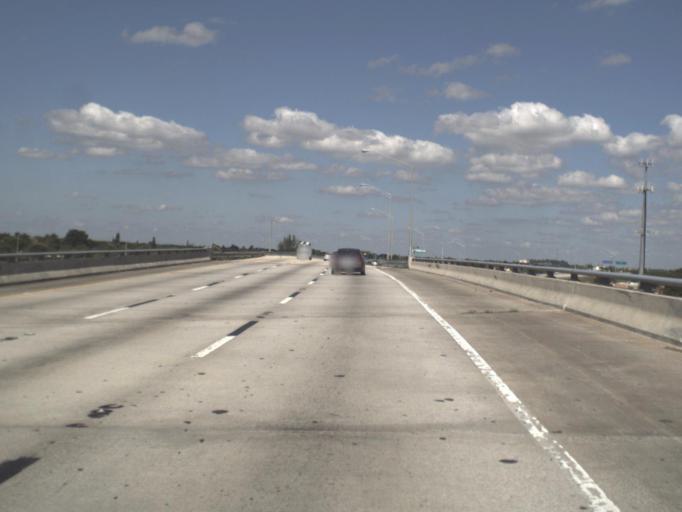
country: US
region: Florida
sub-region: Miami-Dade County
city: Three Lakes
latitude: 25.6503
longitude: -80.3847
